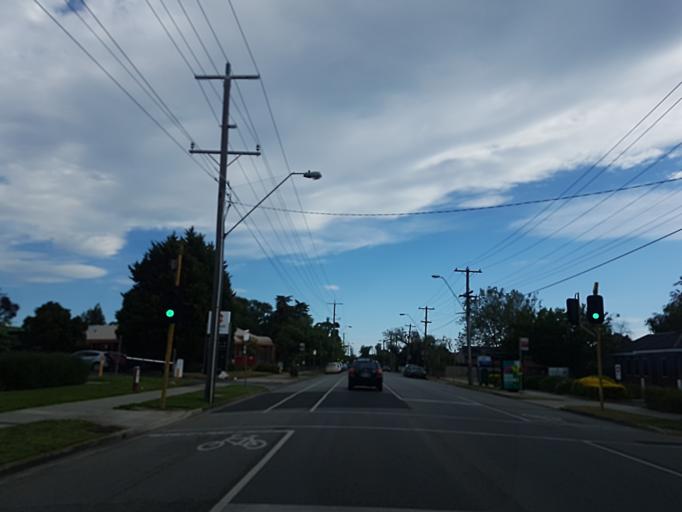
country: AU
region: Victoria
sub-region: Glen Eira
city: Caulfield
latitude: -37.8816
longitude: 145.0158
